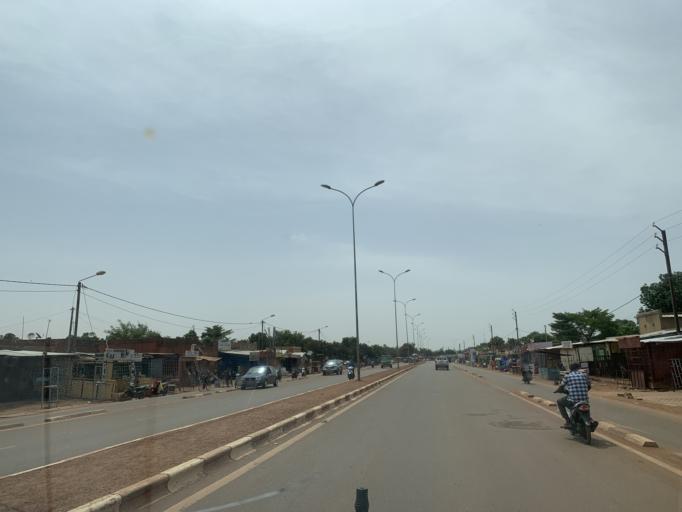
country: BF
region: Centre
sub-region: Kadiogo Province
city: Ouagadougou
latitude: 12.3394
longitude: -1.5143
